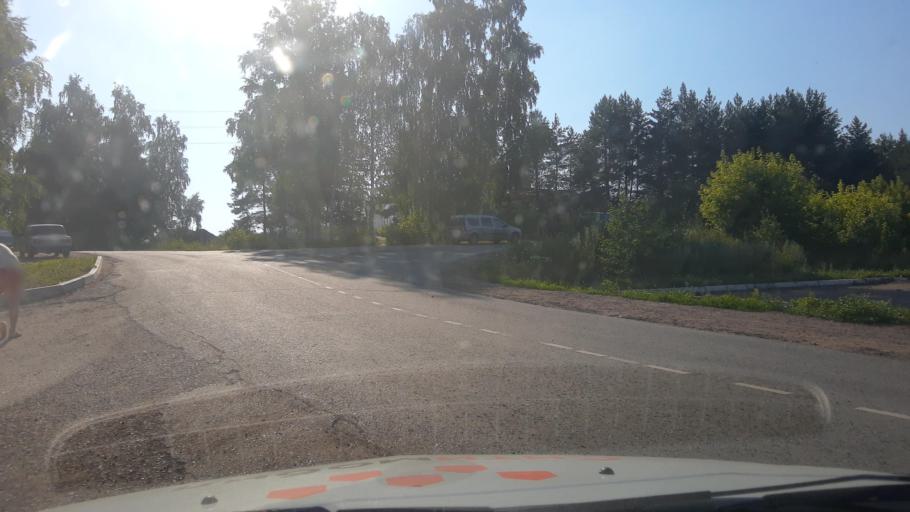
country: RU
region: Bashkortostan
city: Avdon
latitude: 54.6155
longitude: 55.6397
